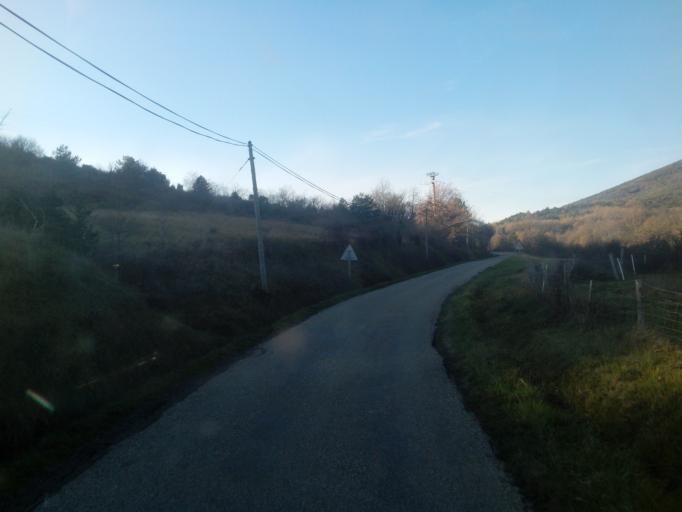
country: FR
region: Languedoc-Roussillon
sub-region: Departement des Pyrenees-Orientales
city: Saint-Paul-de-Fenouillet
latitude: 42.8618
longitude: 2.4586
